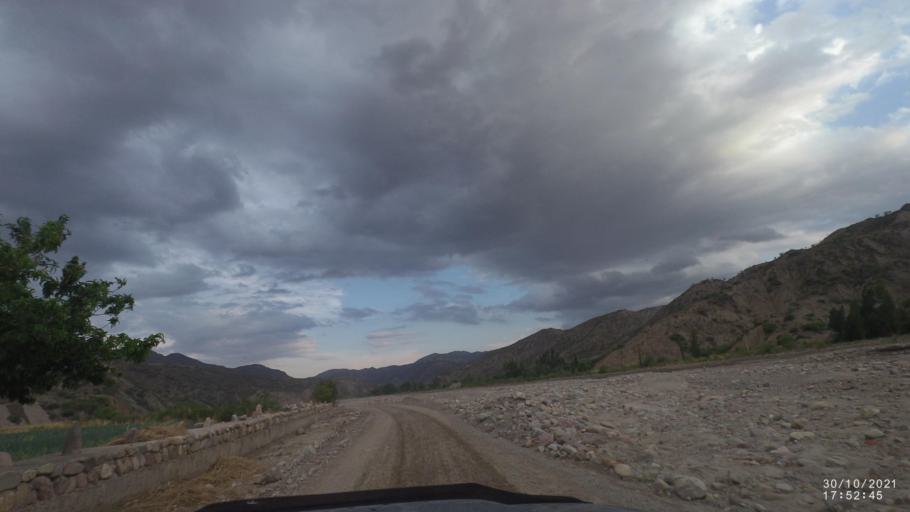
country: BO
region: Cochabamba
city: Sipe Sipe
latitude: -17.5381
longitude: -66.4981
